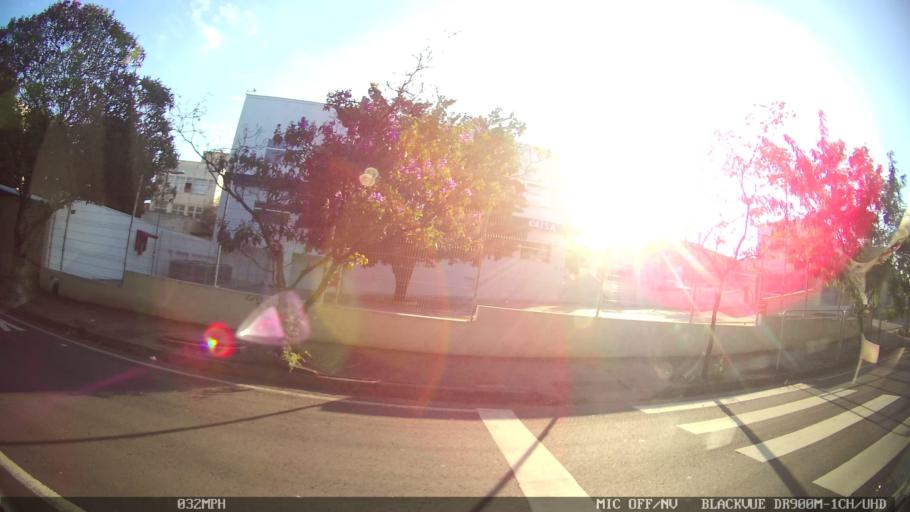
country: BR
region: Sao Paulo
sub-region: Piracicaba
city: Piracicaba
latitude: -22.7092
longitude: -47.6528
